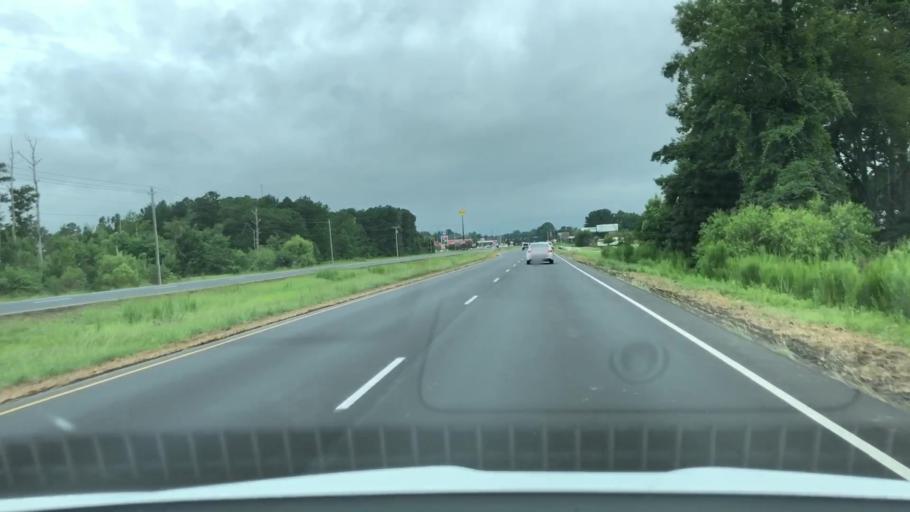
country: US
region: North Carolina
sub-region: Lenoir County
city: Kinston
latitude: 35.2497
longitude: -77.5957
